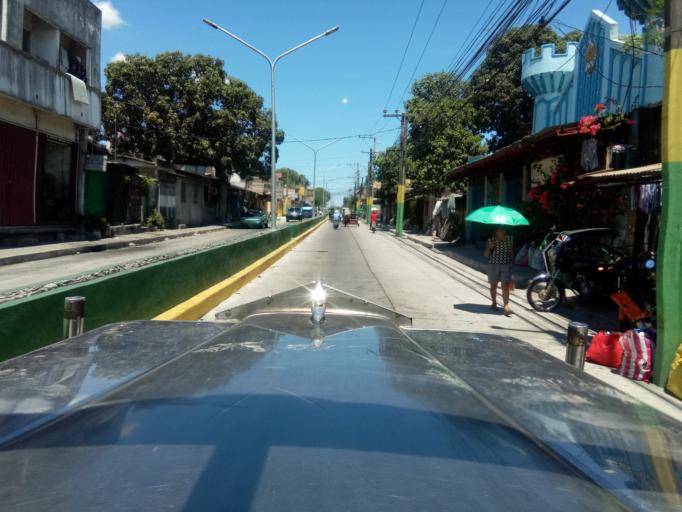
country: PH
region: Calabarzon
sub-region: Province of Cavite
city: Dasmarinas
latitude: 14.3181
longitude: 120.9698
